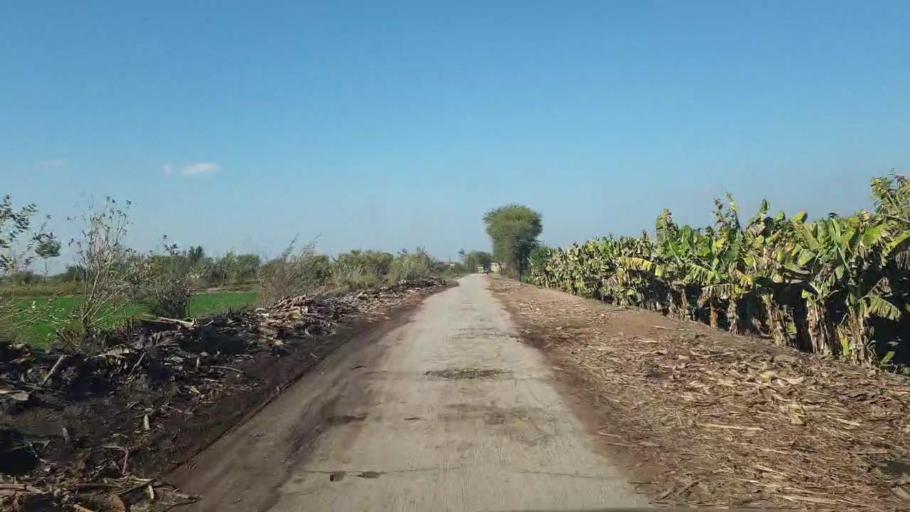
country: PK
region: Sindh
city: Shahdadpur
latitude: 25.9139
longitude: 68.5332
